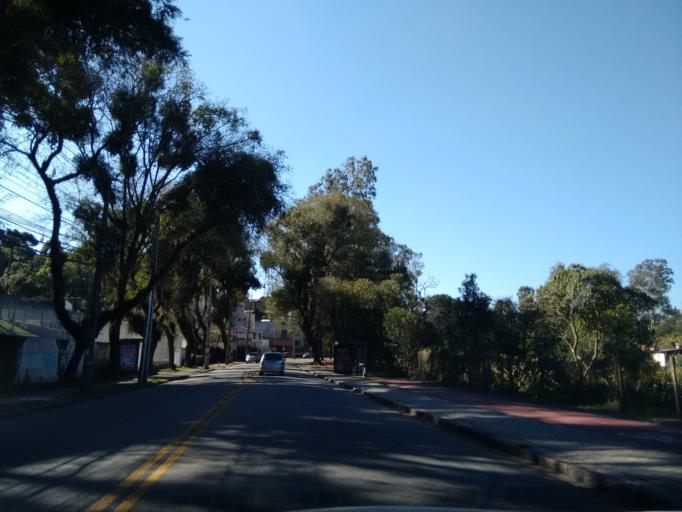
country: BR
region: Parana
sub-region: Curitiba
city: Curitiba
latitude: -25.3934
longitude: -49.2697
